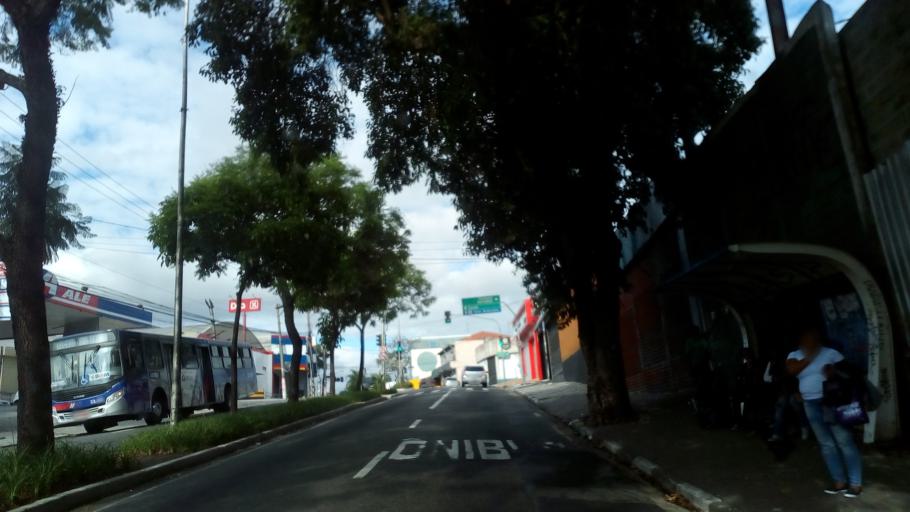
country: BR
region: Sao Paulo
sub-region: Guarulhos
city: Guarulhos
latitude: -23.4621
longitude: -46.5248
